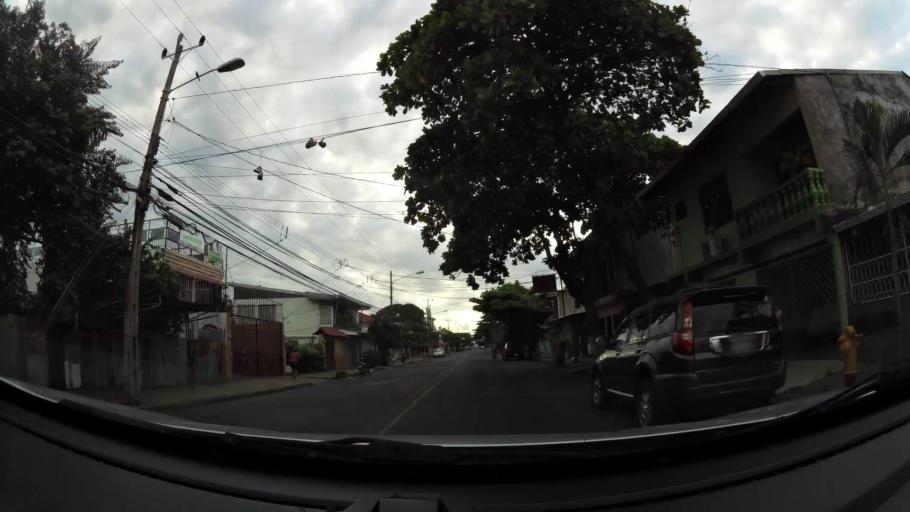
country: CR
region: Puntarenas
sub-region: Canton Central de Puntarenas
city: Puntarenas
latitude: 9.9765
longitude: -84.8429
